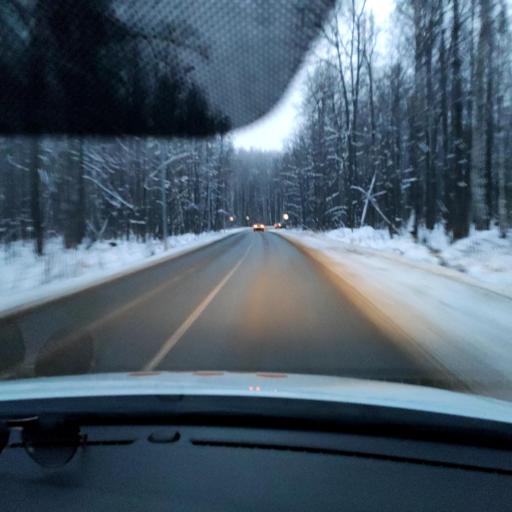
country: RU
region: Tatarstan
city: Vysokaya Gora
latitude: 55.9348
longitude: 49.1721
